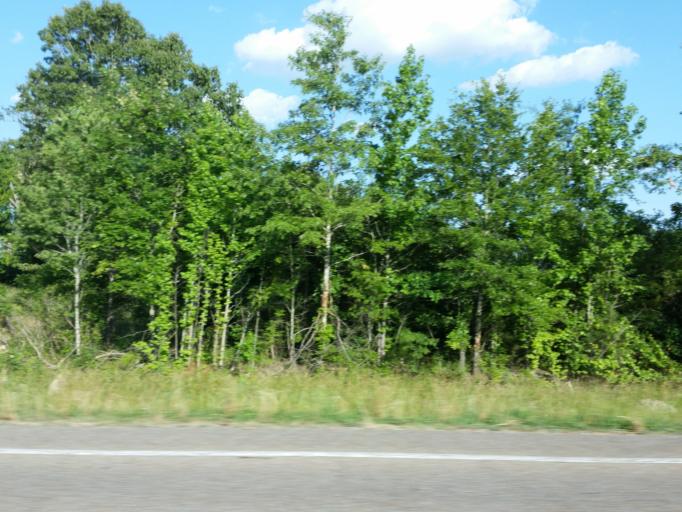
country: US
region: Mississippi
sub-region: Calhoun County
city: Calhoun City
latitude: 33.8183
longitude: -89.3432
